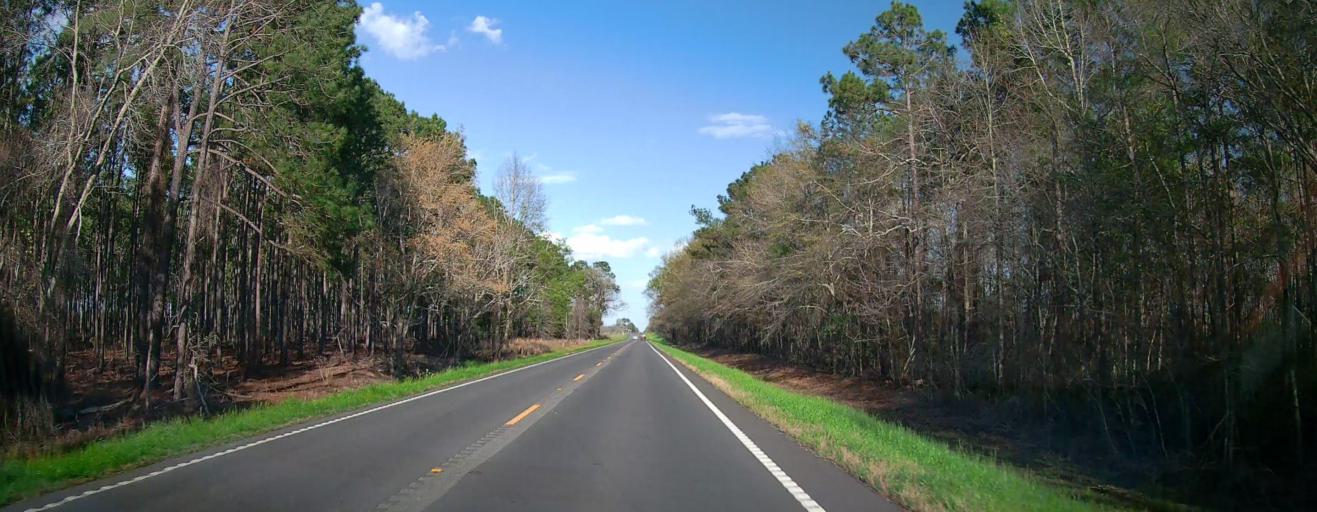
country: US
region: Georgia
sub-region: Montgomery County
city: Mount Vernon
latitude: 32.1849
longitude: -82.5375
